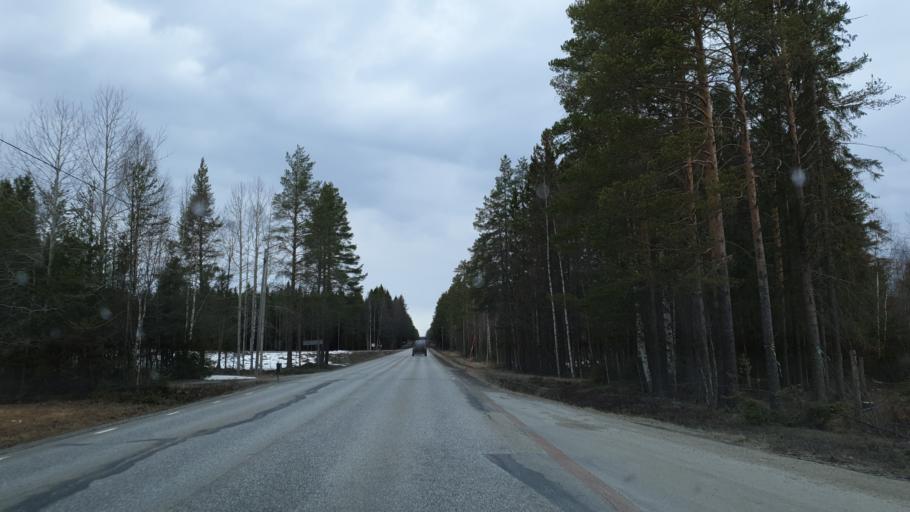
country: SE
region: Vaesterbotten
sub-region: Skelleftea Kommun
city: Viken
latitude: 64.6516
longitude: 20.9553
